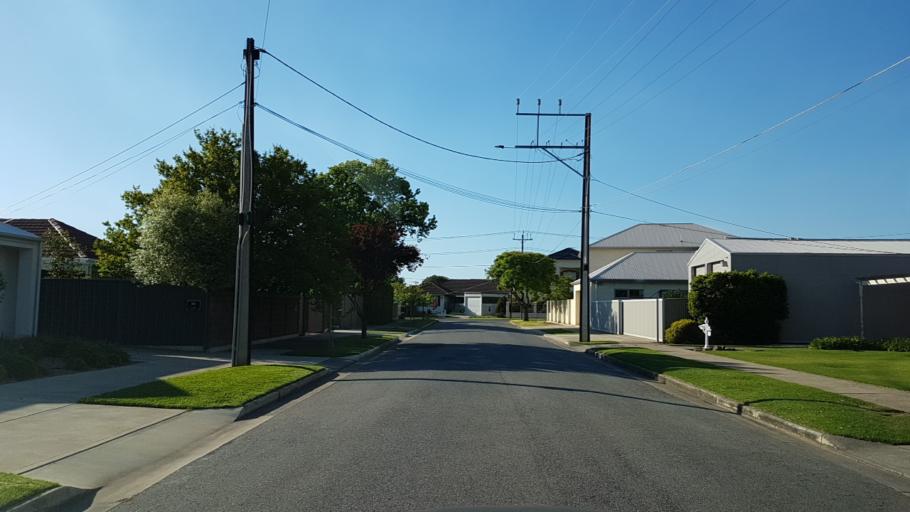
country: AU
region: South Australia
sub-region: Charles Sturt
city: Seaton
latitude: -34.9223
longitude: 138.5180
